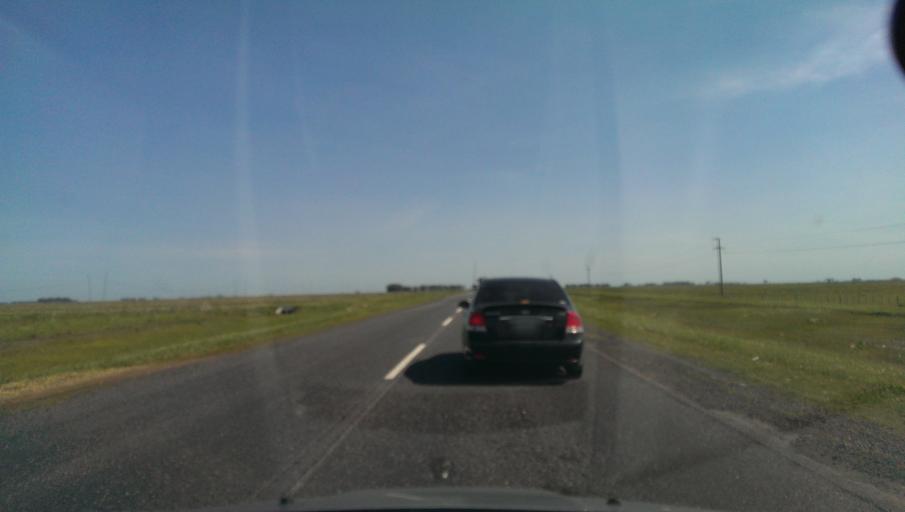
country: AR
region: Buenos Aires
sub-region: Partido de Azul
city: Azul
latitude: -36.5888
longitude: -59.6517
